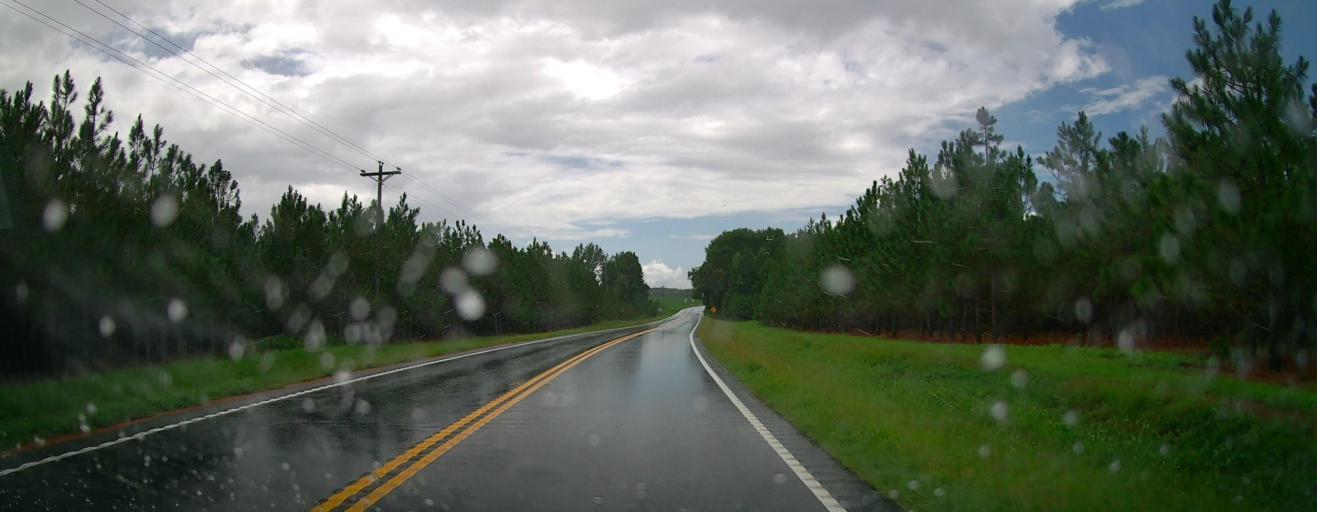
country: US
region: Georgia
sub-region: Pulaski County
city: Hawkinsville
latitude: 32.1910
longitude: -83.5196
